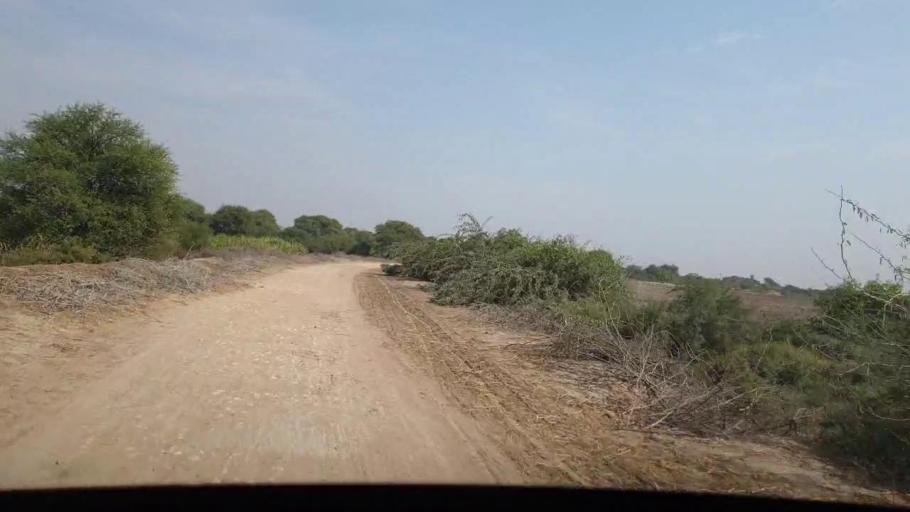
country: PK
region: Sindh
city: Chuhar Jamali
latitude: 24.2692
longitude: 67.9200
